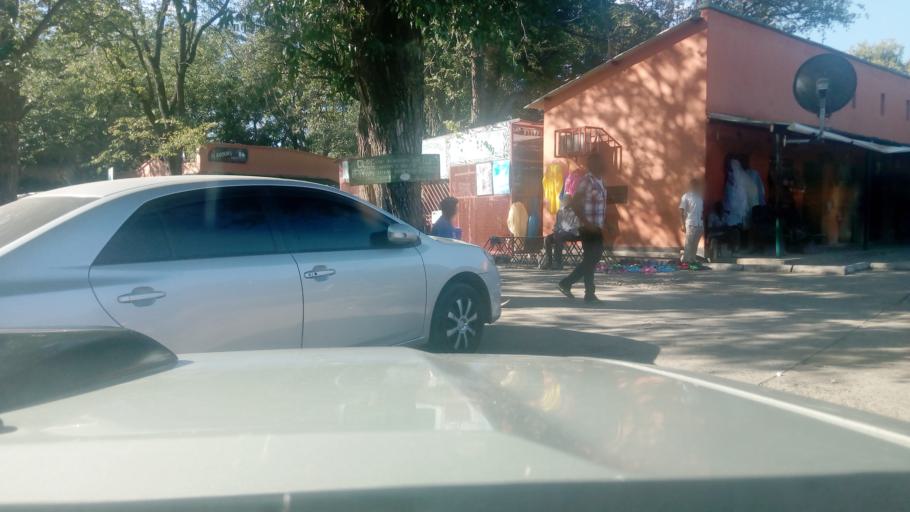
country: ZW
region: Matabeleland North
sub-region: Hwange District
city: Victoria Falls
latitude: -17.9269
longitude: 25.8643
